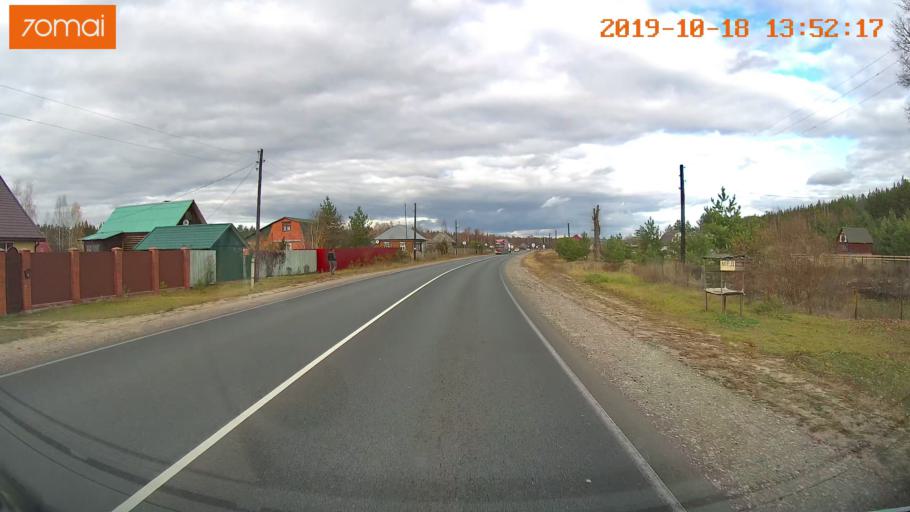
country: RU
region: Moskovskaya
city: Radovitskiy
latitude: 55.0284
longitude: 39.9669
